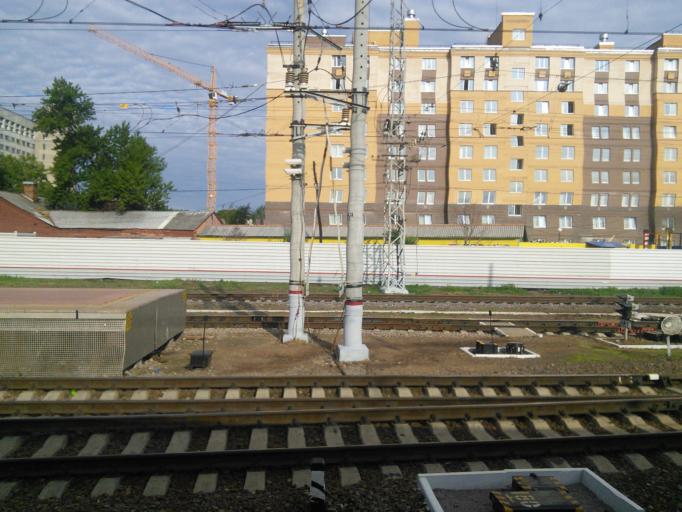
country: RU
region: Leningrad
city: Finlyandskiy
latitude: 59.9598
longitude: 30.3584
